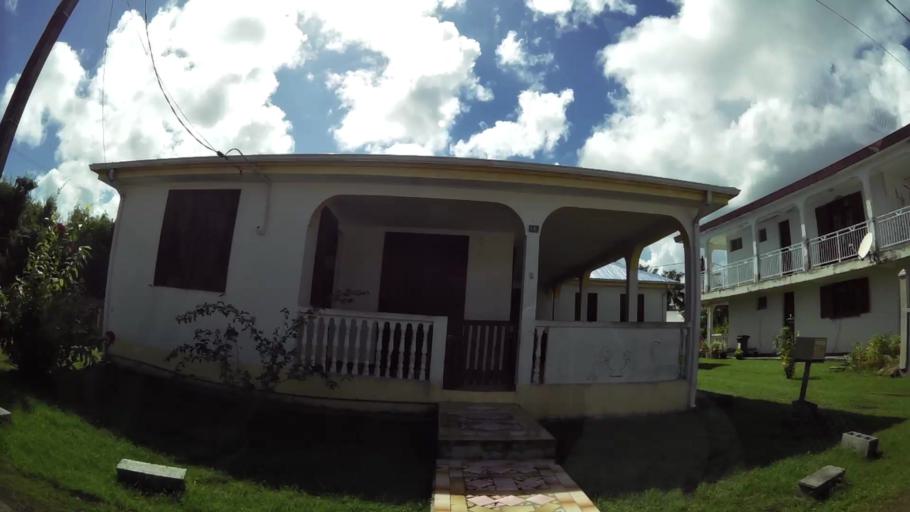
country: GP
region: Guadeloupe
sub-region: Guadeloupe
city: Anse-Bertrand
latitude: 16.4688
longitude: -61.5052
